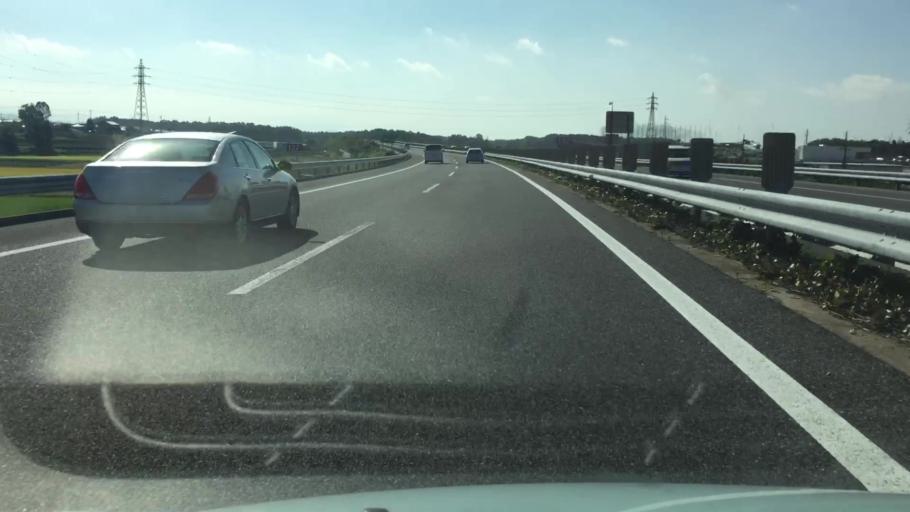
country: JP
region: Tochigi
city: Mooka
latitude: 36.4368
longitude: 139.9703
